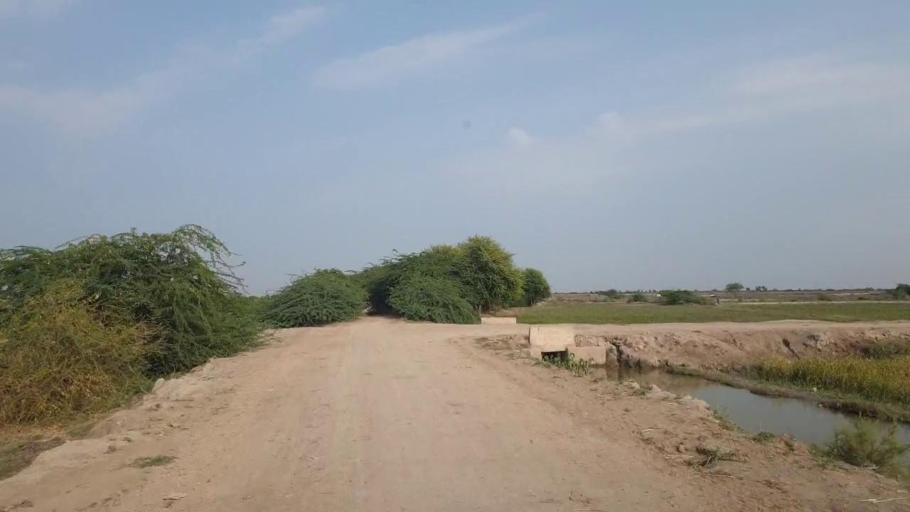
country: PK
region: Sindh
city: Kadhan
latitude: 24.4603
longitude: 68.8122
